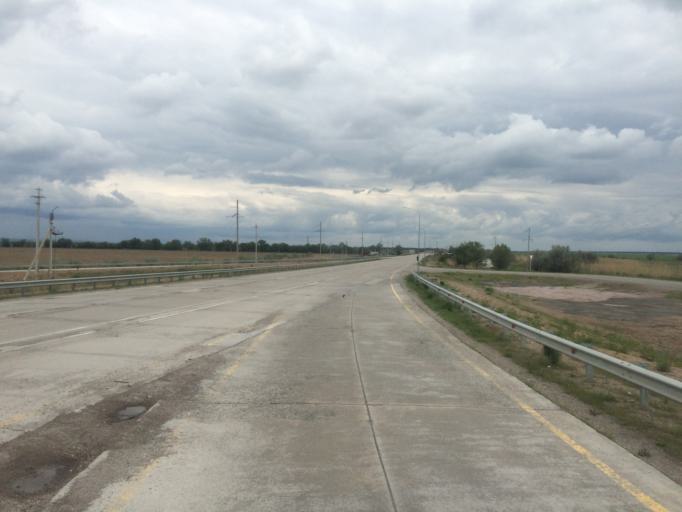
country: KG
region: Chuy
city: Sokuluk
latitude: 43.2732
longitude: 74.2348
